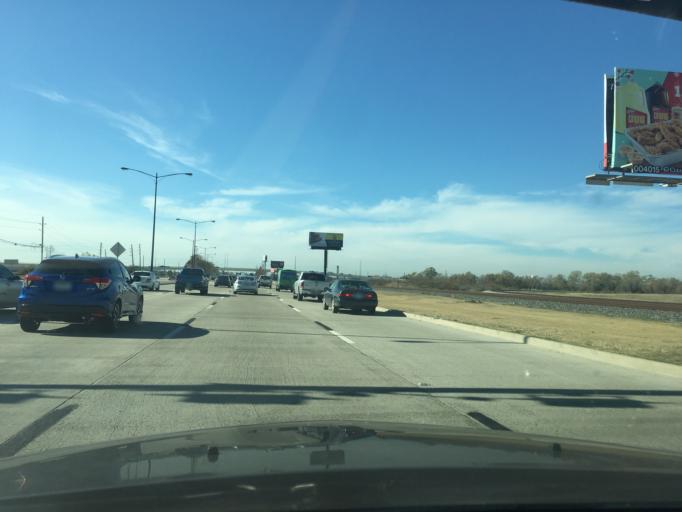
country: US
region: Texas
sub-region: Fort Bend County
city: Sugar Land
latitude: 29.6163
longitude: -95.6441
